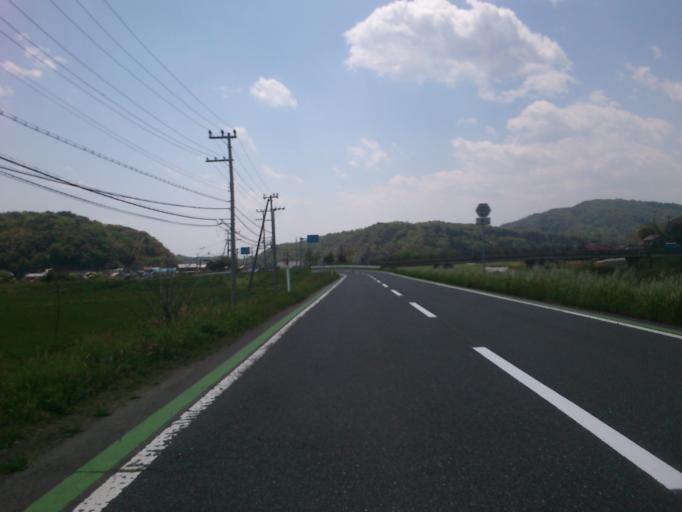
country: JP
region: Kyoto
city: Miyazu
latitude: 35.7155
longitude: 135.1067
